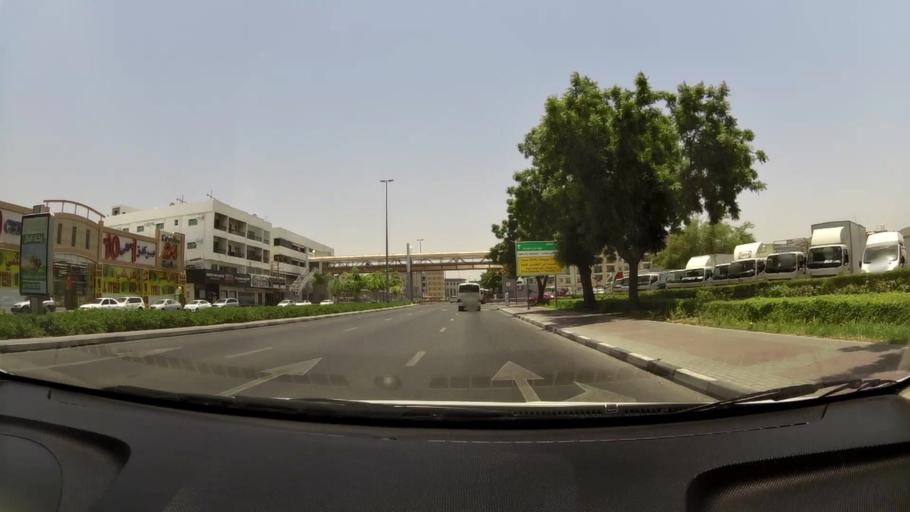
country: AE
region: Ash Shariqah
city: Sharjah
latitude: 25.2737
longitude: 55.3295
